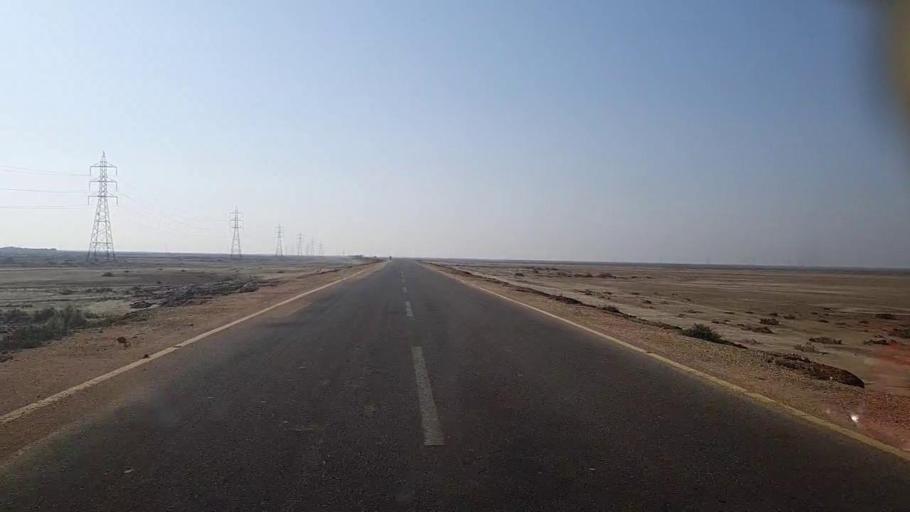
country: PK
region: Sindh
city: Mirpur Sakro
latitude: 24.6122
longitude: 67.4970
